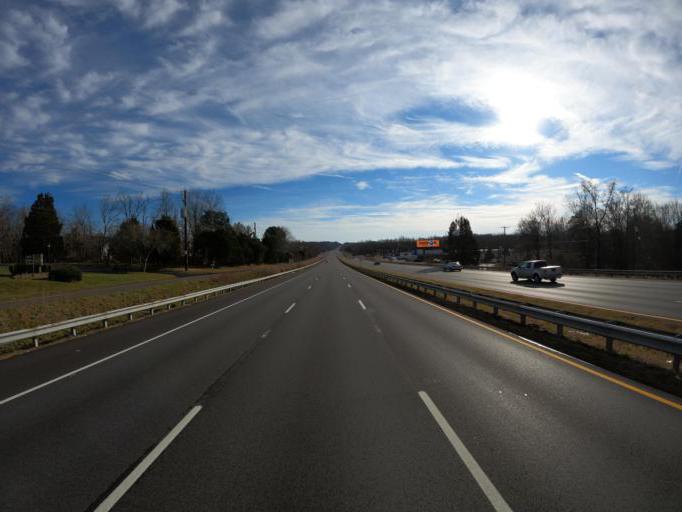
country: US
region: Maryland
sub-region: Prince George's County
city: Friendly
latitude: 38.7396
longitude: -76.9915
